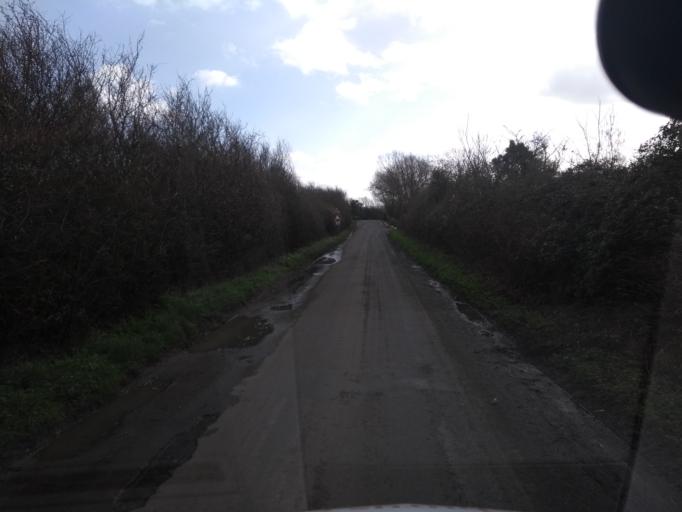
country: GB
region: England
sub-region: Somerset
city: Curry Rivel
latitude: 50.9907
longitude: -2.8549
